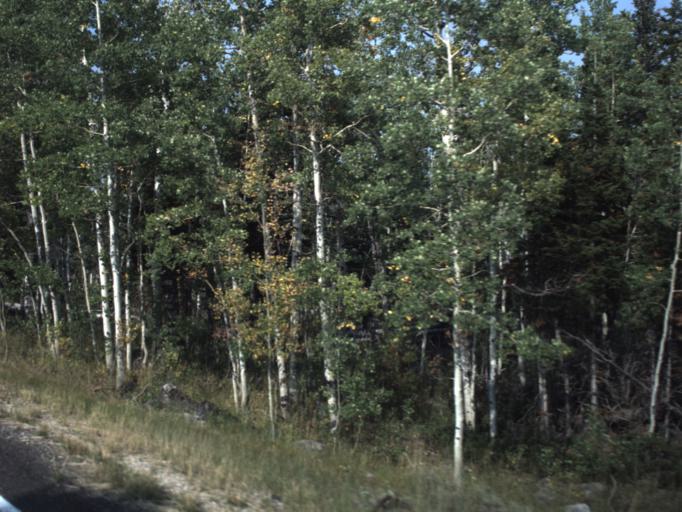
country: US
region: Wyoming
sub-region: Uinta County
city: Evanston
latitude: 40.8420
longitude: -110.8475
